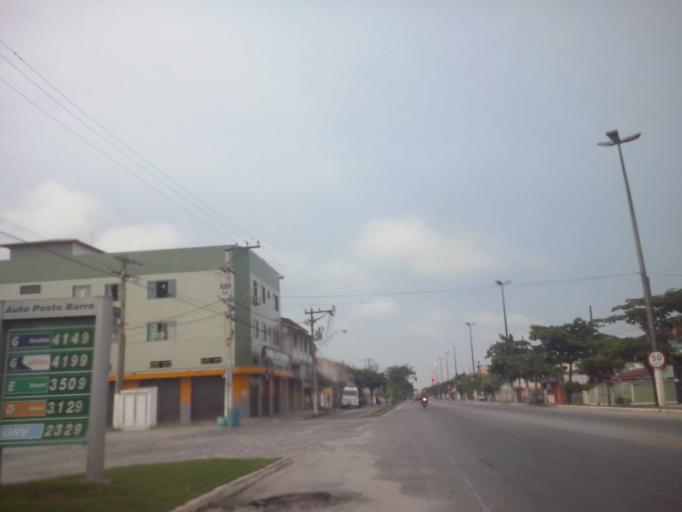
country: BR
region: Rio de Janeiro
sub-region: Rio Das Ostras
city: Rio das Ostras
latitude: -22.5764
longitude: -41.9869
